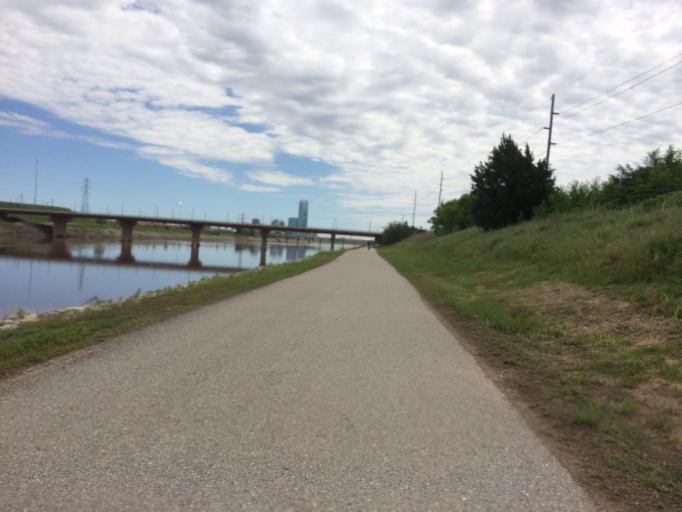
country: US
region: Oklahoma
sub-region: Oklahoma County
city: Oklahoma City
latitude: 35.4583
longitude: -97.5577
